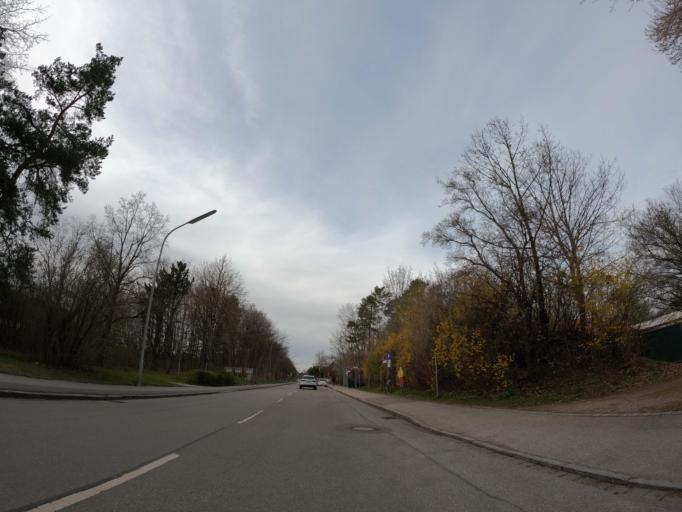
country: DE
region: Bavaria
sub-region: Upper Bavaria
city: Ottobrunn
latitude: 48.0656
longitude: 11.6535
